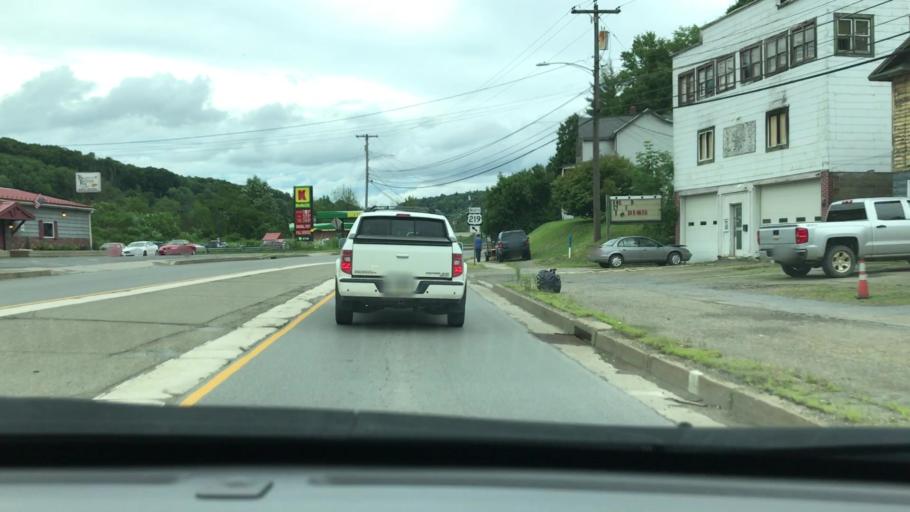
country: US
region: Pennsylvania
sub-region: Elk County
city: Johnsonburg
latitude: 41.4809
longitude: -78.6712
